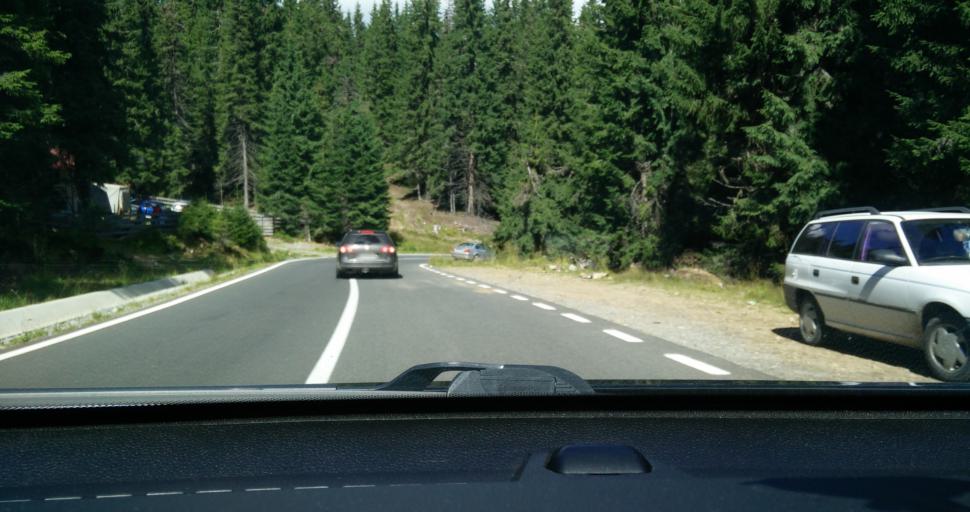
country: RO
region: Hunedoara
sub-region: Oras Petrila
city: Petrila
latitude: 45.4799
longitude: 23.6343
